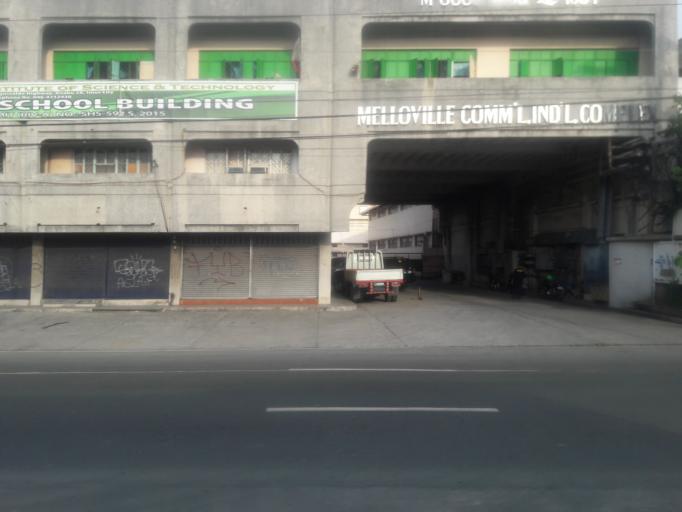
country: PH
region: Calabarzon
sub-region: Province of Cavite
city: Imus
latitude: 14.3866
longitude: 120.9395
